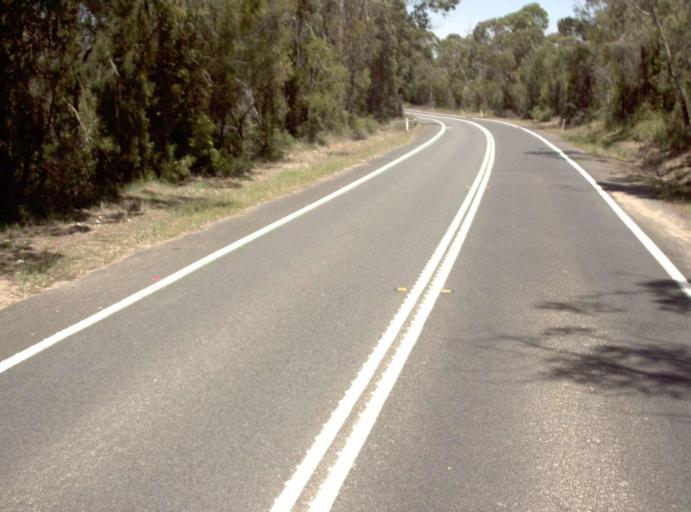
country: AU
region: Victoria
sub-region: East Gippsland
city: Lakes Entrance
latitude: -37.8298
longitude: 148.0318
